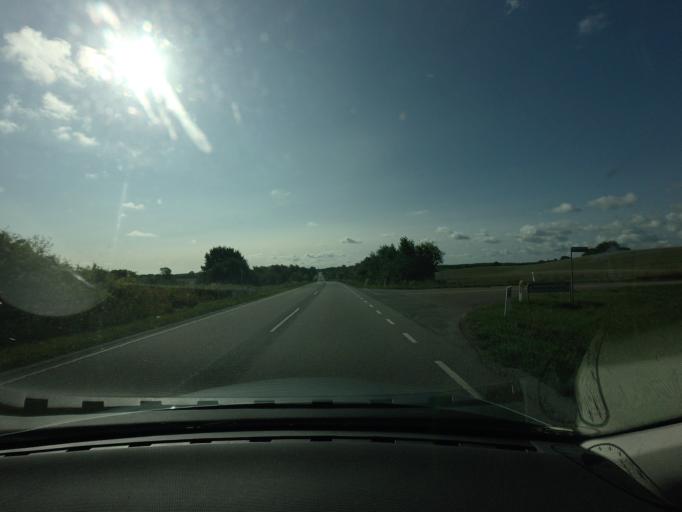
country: DK
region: Zealand
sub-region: Vordingborg Kommune
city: Praesto
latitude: 55.0523
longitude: 12.0899
